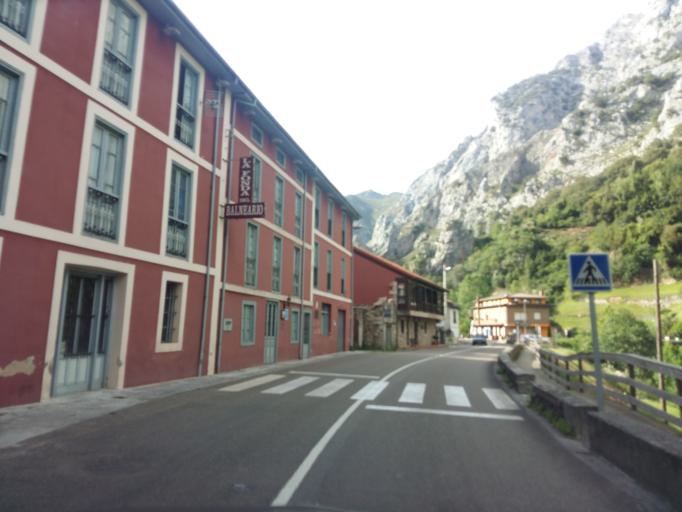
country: ES
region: Cantabria
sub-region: Provincia de Cantabria
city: Tresviso
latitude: 43.2530
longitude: -4.6130
